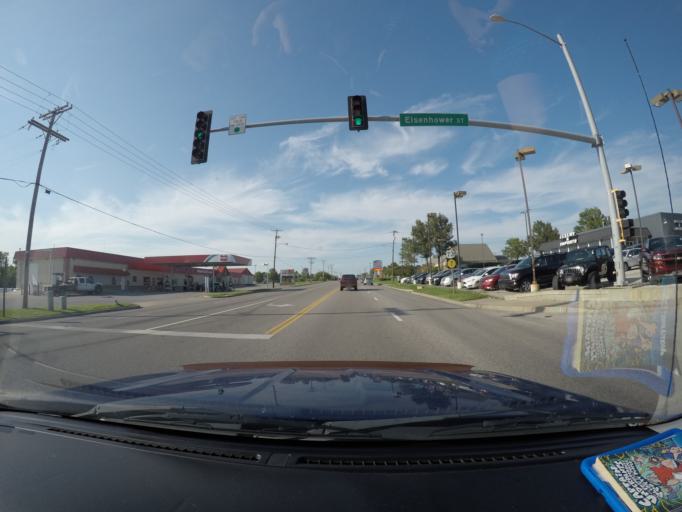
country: US
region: Kansas
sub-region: Leavenworth County
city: Lansing
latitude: 39.2671
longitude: -94.8998
